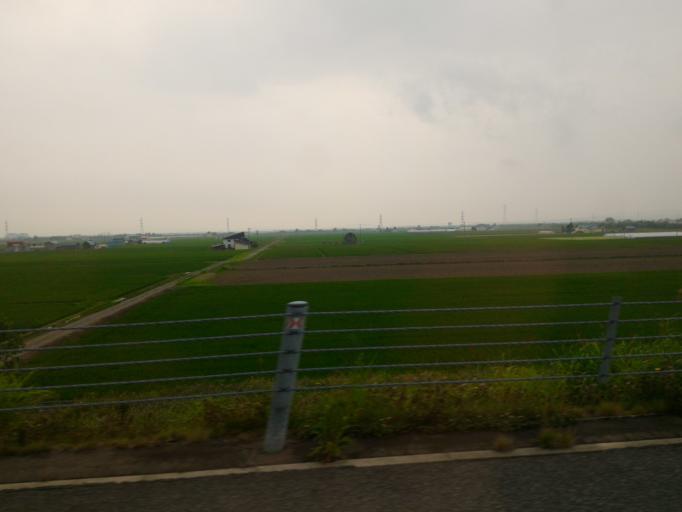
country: JP
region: Hokkaido
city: Fukagawa
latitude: 43.8017
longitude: 141.9176
